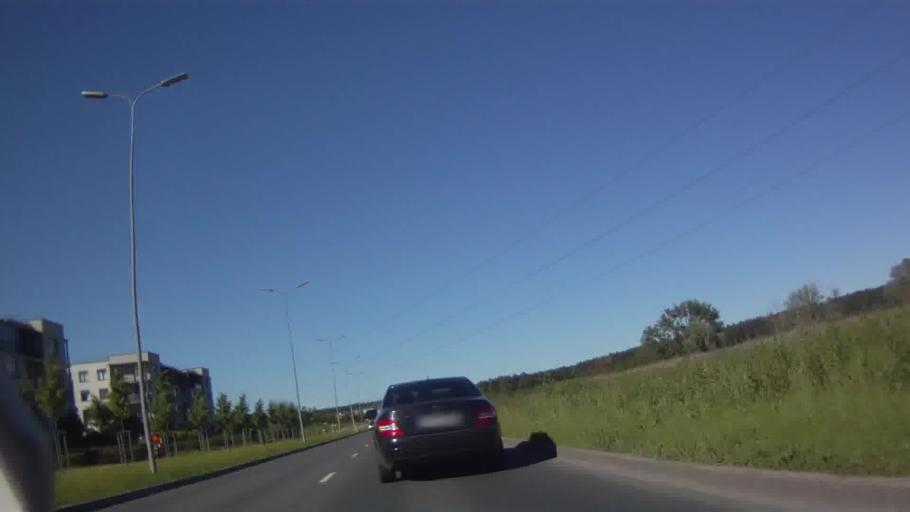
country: LV
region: Stopini
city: Ulbroka
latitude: 56.9504
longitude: 24.2485
